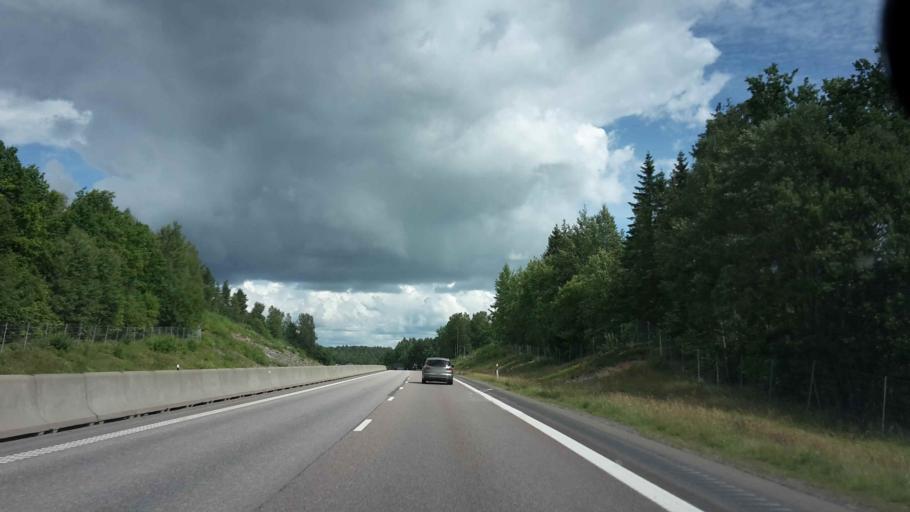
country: SE
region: OEstergoetland
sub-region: Norrkopings Kommun
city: Kimstad
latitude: 58.5010
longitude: 15.9839
